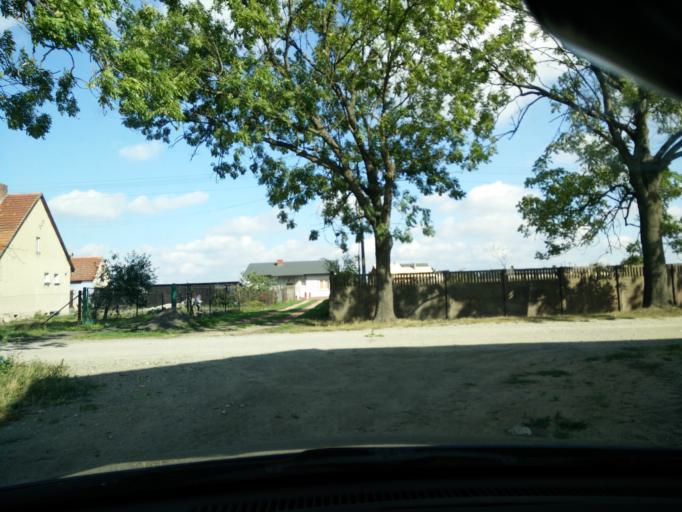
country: PL
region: Greater Poland Voivodeship
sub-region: Powiat sredzki
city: Sroda Wielkopolska
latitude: 52.2634
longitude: 17.3100
